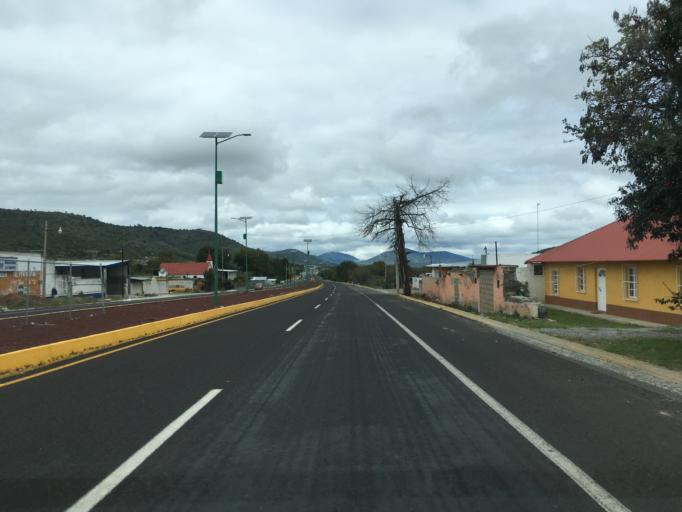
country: MX
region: Hidalgo
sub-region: Atotonilco el Grande
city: La Estancia
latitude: 20.3179
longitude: -98.6916
